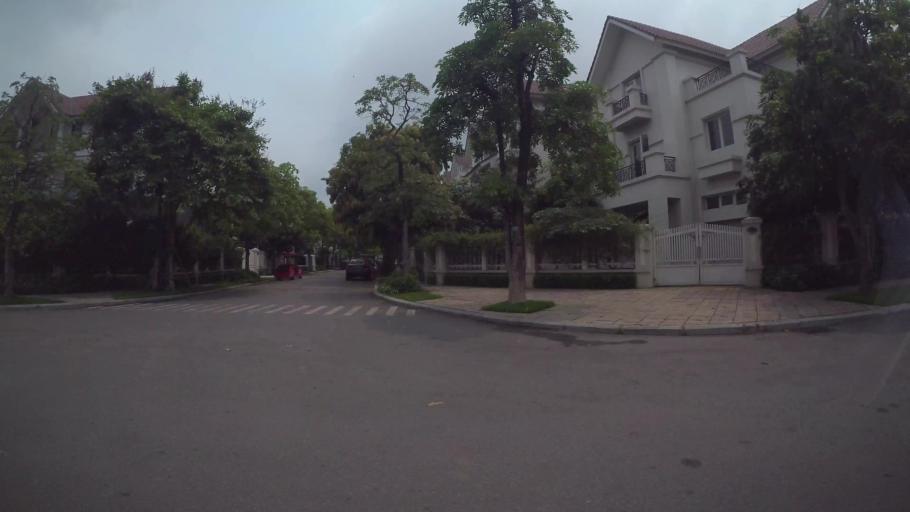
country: VN
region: Ha Noi
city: Trau Quy
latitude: 21.0423
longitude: 105.9161
